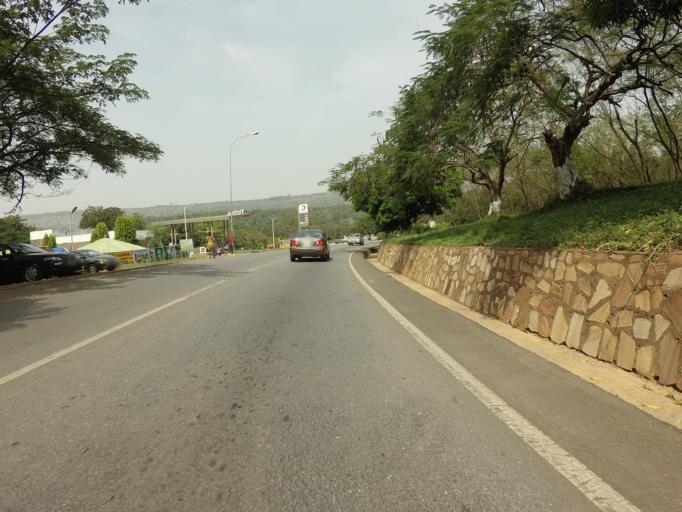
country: GH
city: Akropong
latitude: 6.2716
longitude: 0.0544
